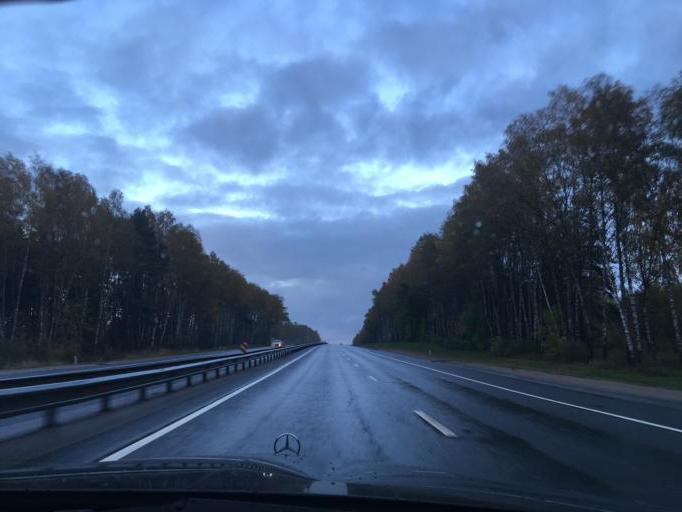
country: RU
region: Smolensk
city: Yartsevo
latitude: 55.0850
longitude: 32.7864
